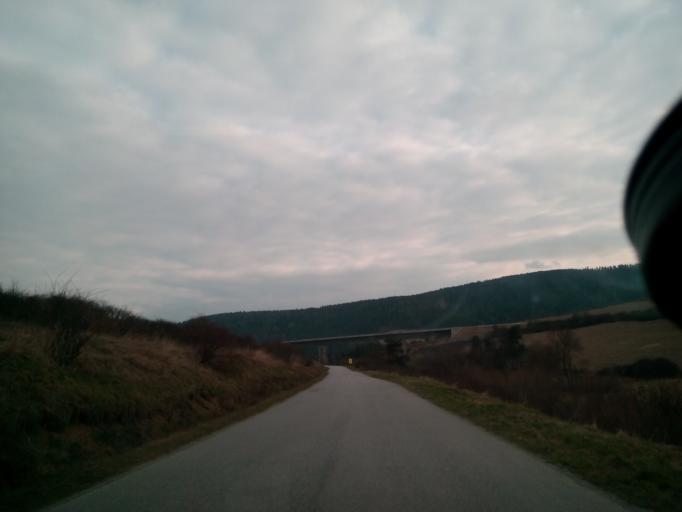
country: SK
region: Presovsky
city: Sabinov
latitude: 49.0320
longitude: 21.0188
